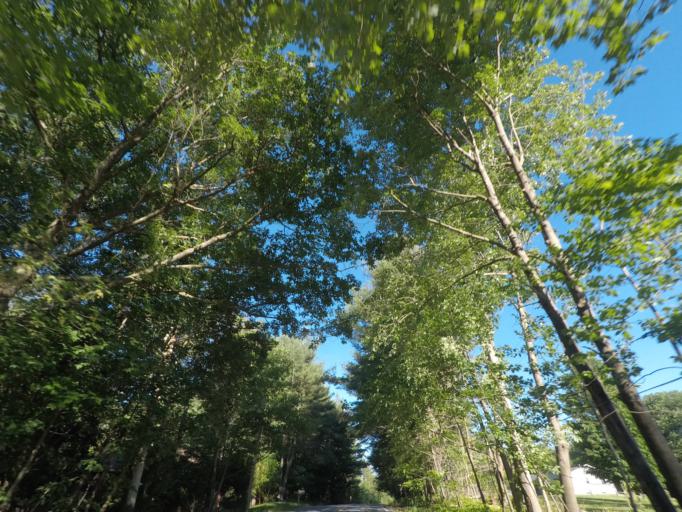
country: US
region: New York
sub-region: Rensselaer County
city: West Sand Lake
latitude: 42.5996
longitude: -73.5985
